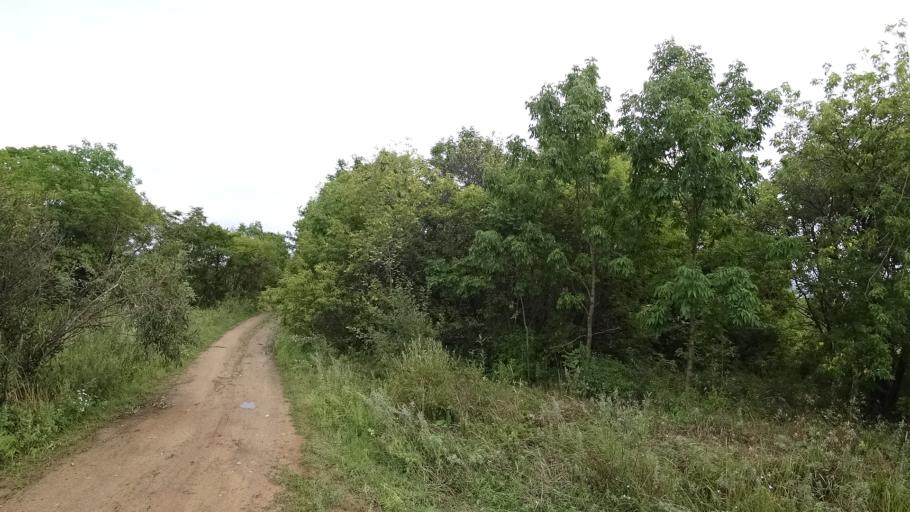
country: RU
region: Primorskiy
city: Rettikhovka
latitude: 44.1356
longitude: 132.6329
